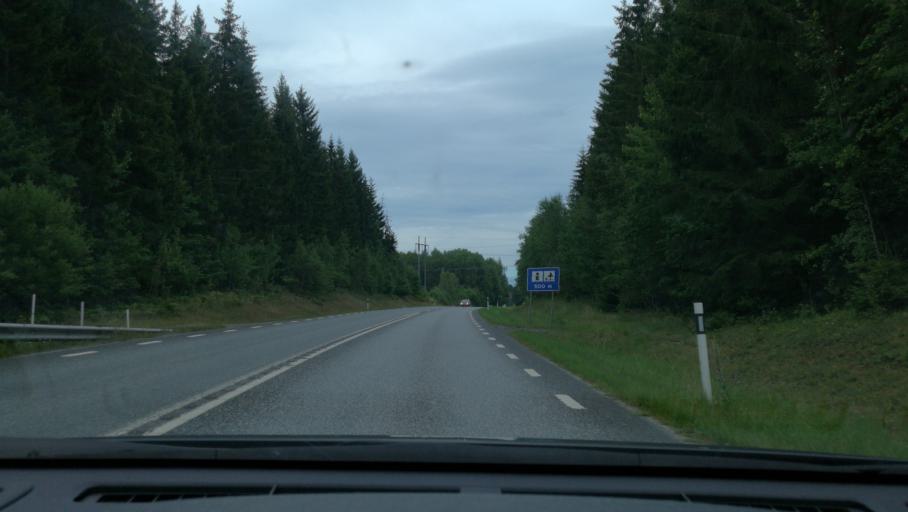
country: SE
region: Soedermanland
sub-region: Katrineholms Kommun
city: Katrineholm
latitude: 58.9633
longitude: 16.1907
